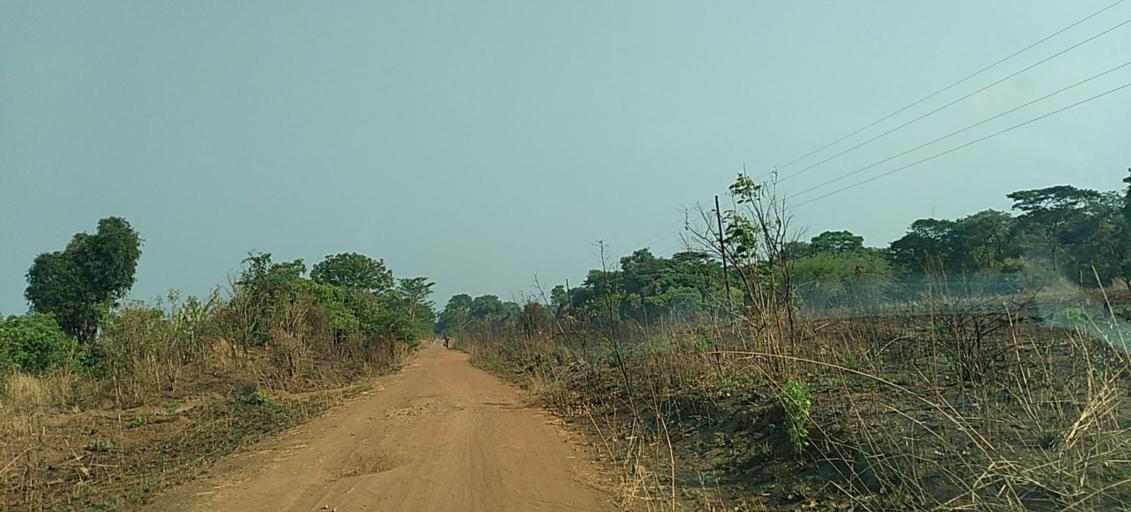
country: ZM
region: Copperbelt
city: Chingola
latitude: -12.8431
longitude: 27.5470
